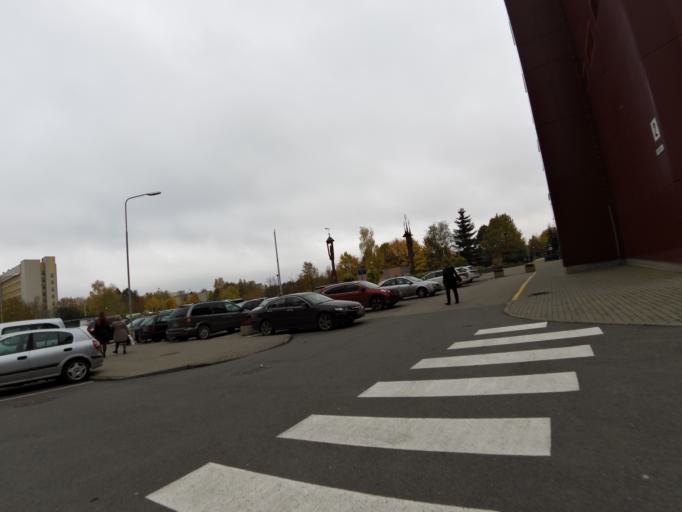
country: LT
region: Vilnius County
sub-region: Vilnius
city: Fabijoniskes
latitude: 54.7525
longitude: 25.2787
